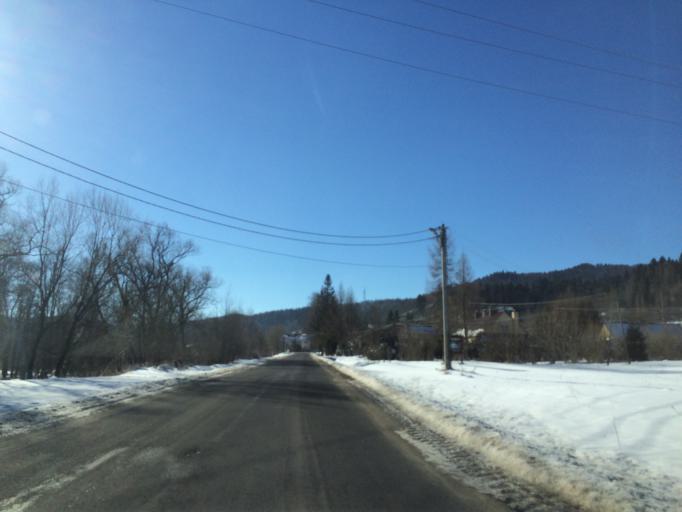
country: PL
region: Subcarpathian Voivodeship
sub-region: Powiat bieszczadzki
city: Lutowiska
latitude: 49.1917
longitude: 22.6837
